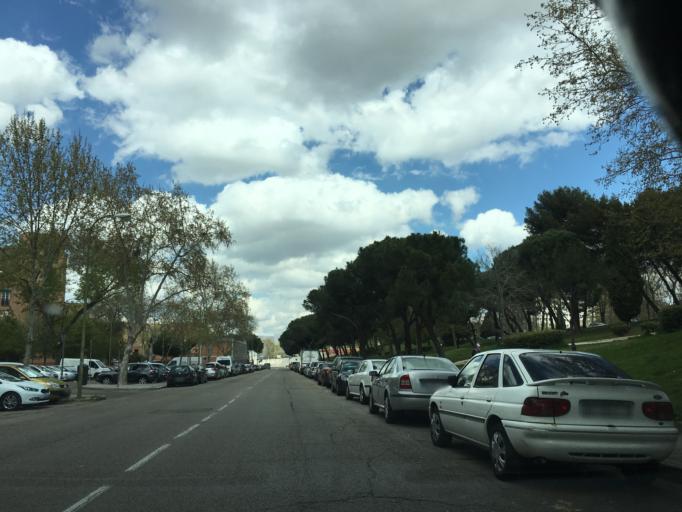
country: ES
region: Madrid
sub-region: Provincia de Madrid
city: San Blas
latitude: 40.4314
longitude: -3.6229
